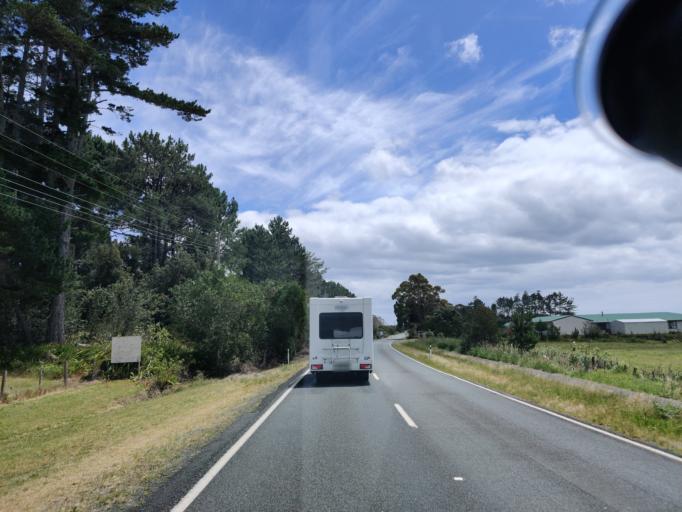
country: NZ
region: Northland
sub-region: Far North District
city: Kaitaia
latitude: -34.7442
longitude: 173.0473
